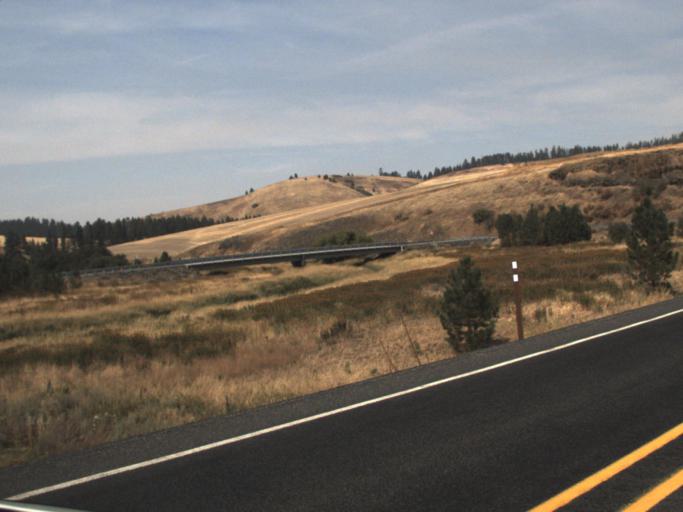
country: US
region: Idaho
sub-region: Benewah County
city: Plummer
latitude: 47.3336
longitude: -117.1924
